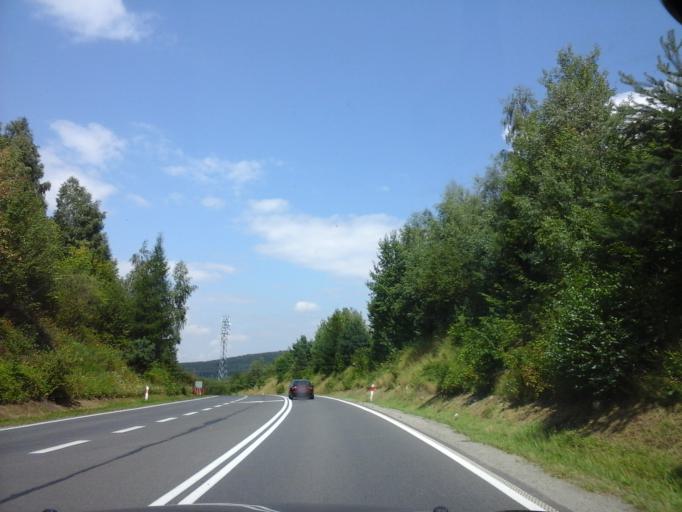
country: PL
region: Lesser Poland Voivodeship
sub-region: Powiat wadowicki
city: Jaroszowice
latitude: 49.8281
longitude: 19.5239
